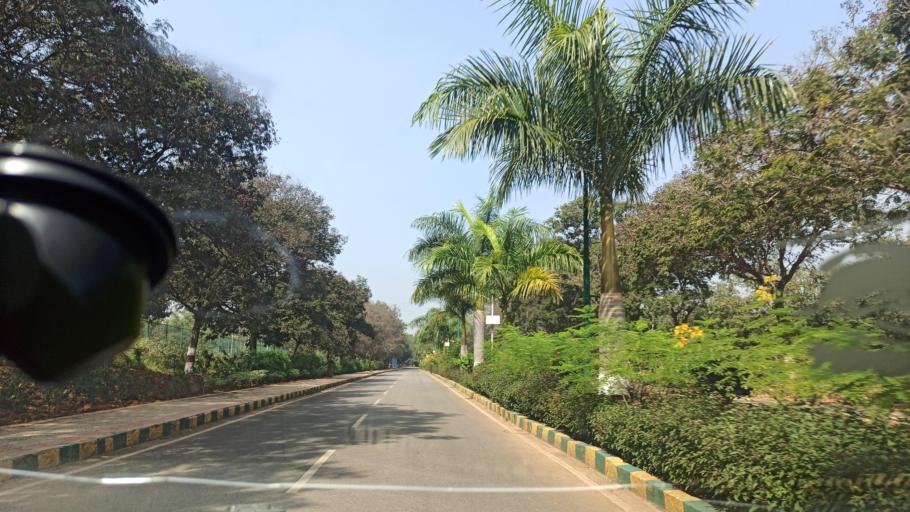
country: IN
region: Karnataka
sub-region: Bangalore Urban
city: Yelahanka
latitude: 13.0762
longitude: 77.5840
